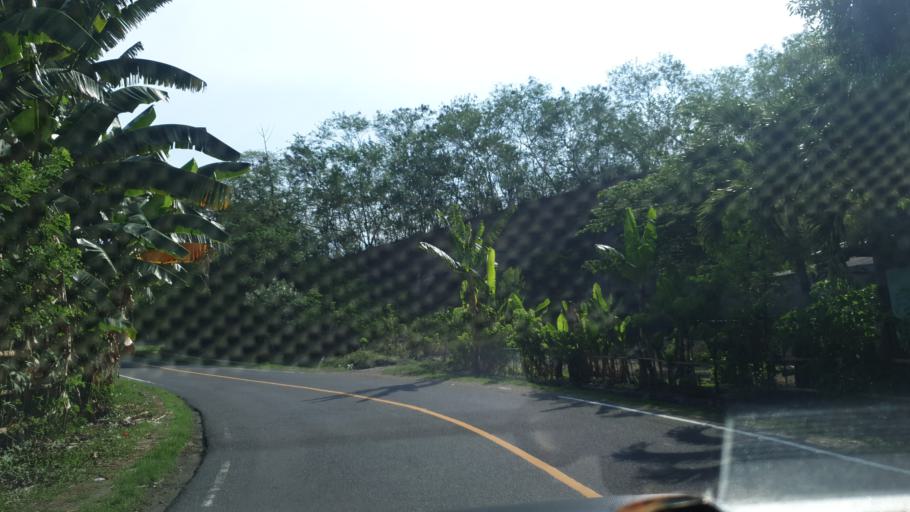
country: ID
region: East Nusa Tenggara
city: Nangalimang
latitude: -8.6575
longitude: 122.2020
